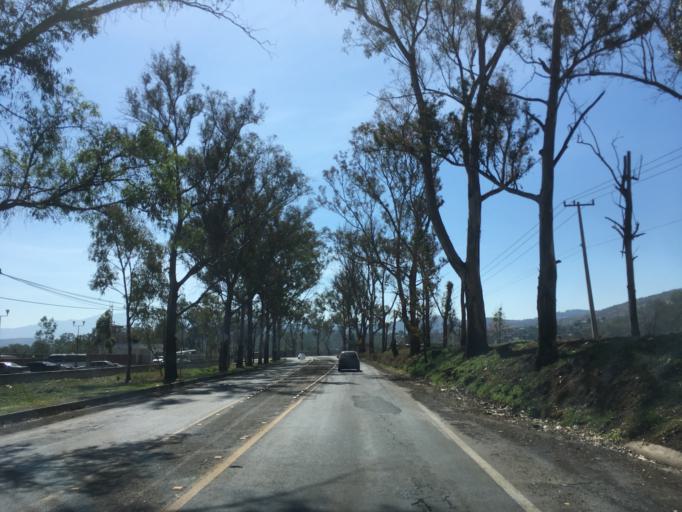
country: MX
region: Michoacan
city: Charo
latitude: 19.6812
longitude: -101.0592
